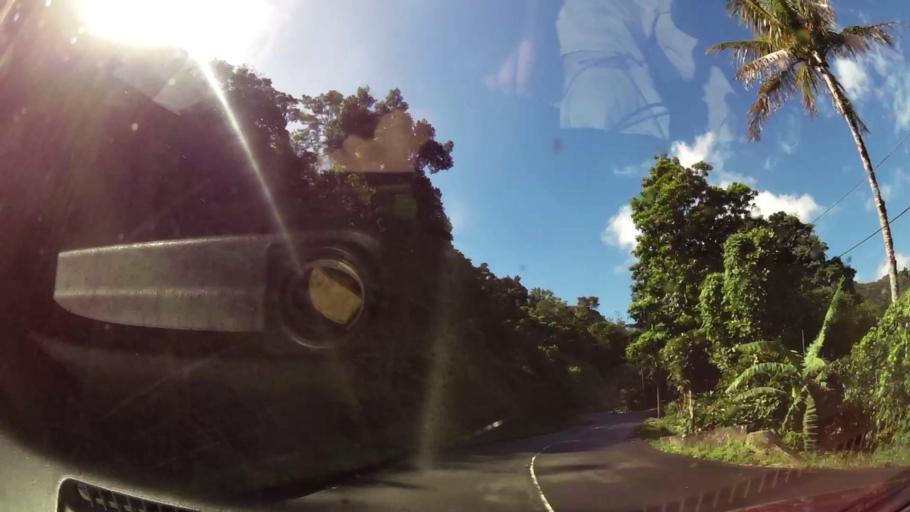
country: DM
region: Saint Paul
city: Pont Casse
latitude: 15.3629
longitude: -61.3537
